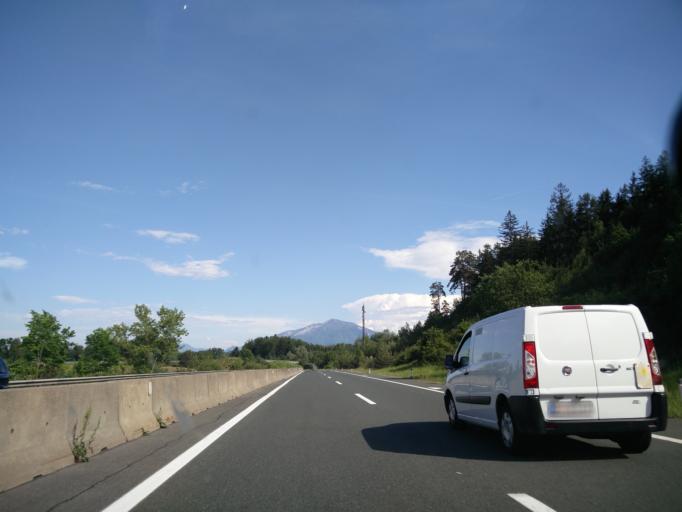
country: AT
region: Carinthia
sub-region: Politischer Bezirk Klagenfurt Land
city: Grafenstein
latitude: 46.6478
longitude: 14.5439
